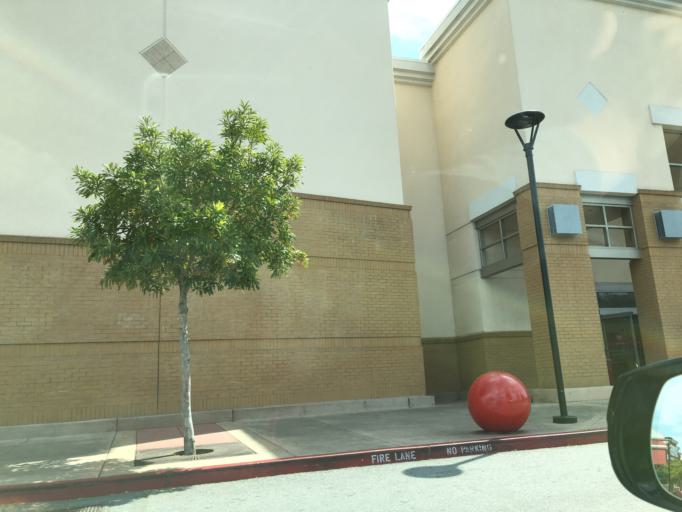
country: US
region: California
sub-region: San Mateo County
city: Foster City
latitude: 37.5590
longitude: -122.2836
